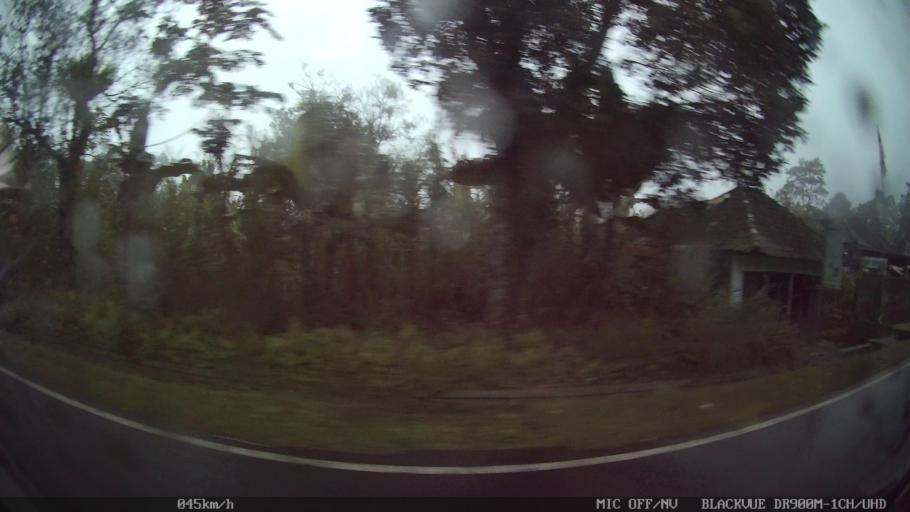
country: ID
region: Bali
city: Banjar Taro Kelod
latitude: -8.3259
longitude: 115.2936
